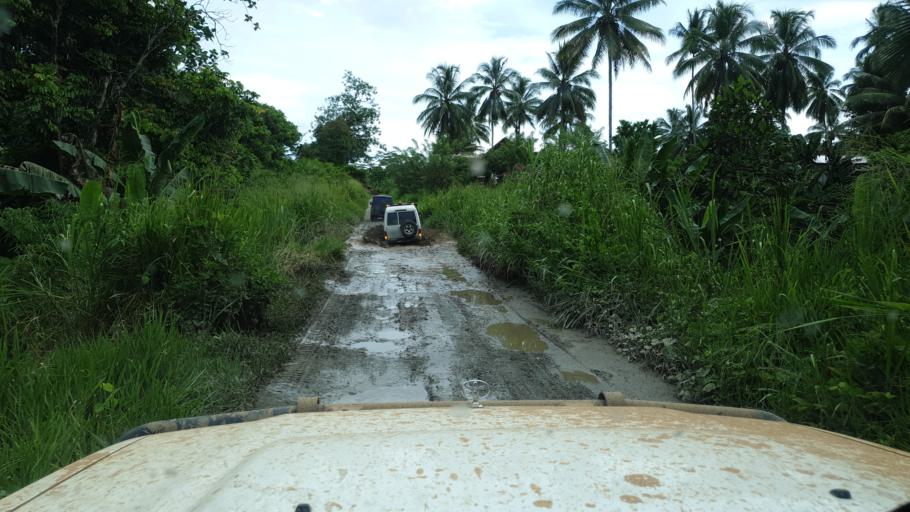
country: PG
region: Northern Province
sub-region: Sohe
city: Kokoda
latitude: -8.9173
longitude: 147.8607
